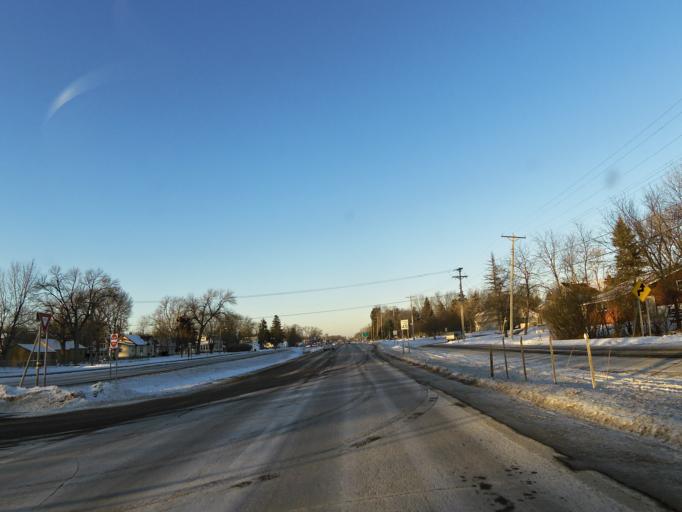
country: US
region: Minnesota
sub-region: Dakota County
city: Farmington
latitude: 44.6366
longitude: -93.1369
